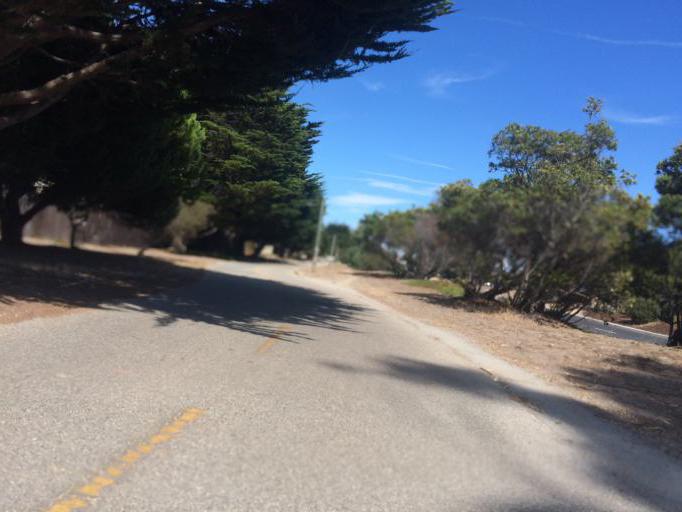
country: US
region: California
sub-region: Monterey County
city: Seaside
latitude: 36.6011
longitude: -121.8691
